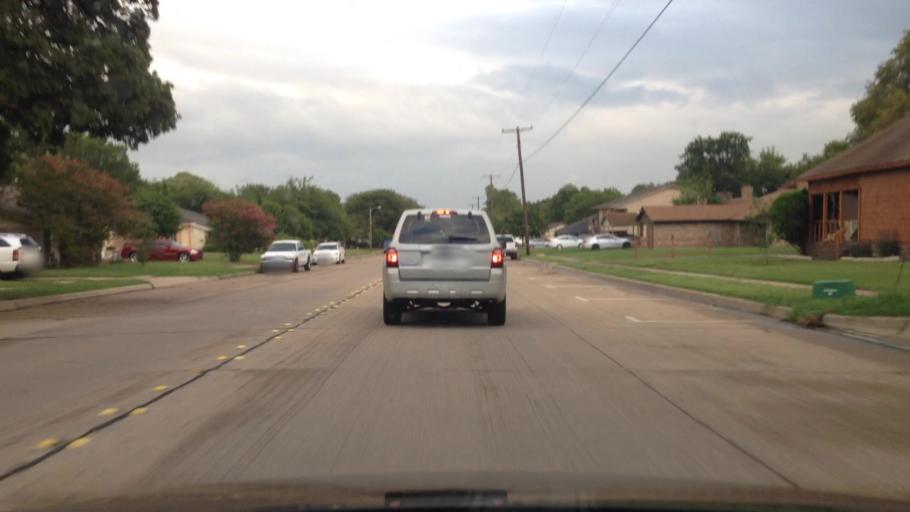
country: US
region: Texas
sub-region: Johnson County
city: Burleson
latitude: 32.5517
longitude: -97.3351
